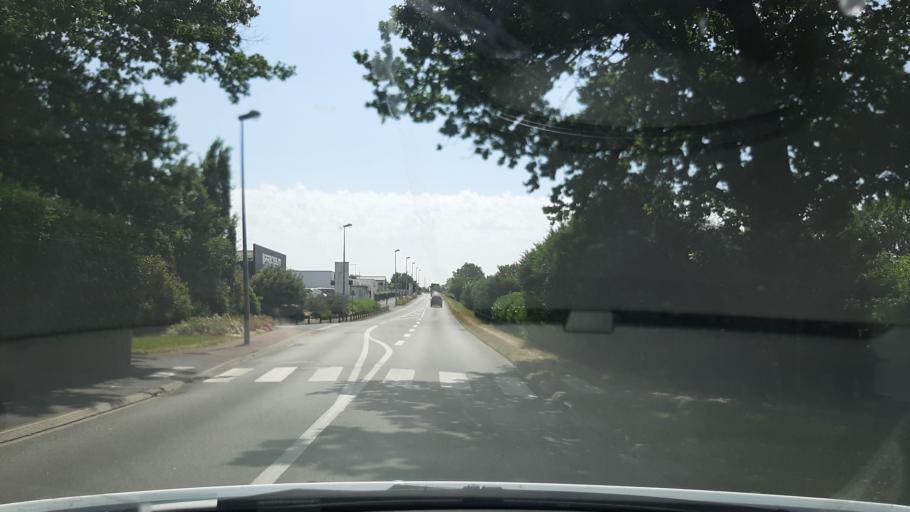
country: FR
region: Pays de la Loire
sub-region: Departement de la Vendee
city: Le Poire-sur-Vie
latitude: 46.7689
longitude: -1.5033
